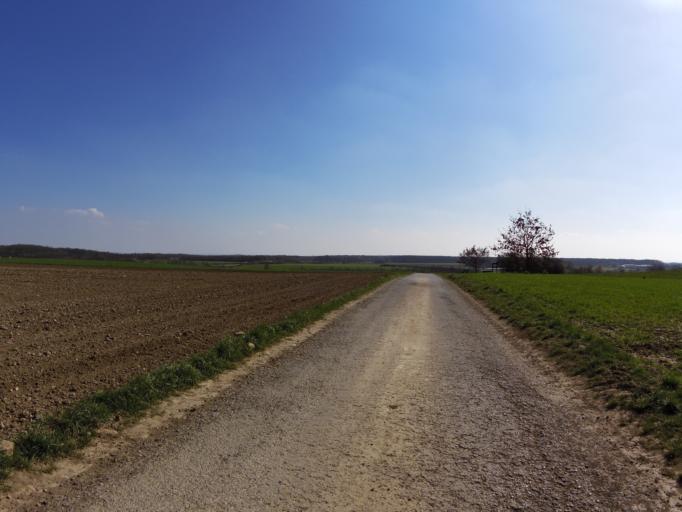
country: DE
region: Bavaria
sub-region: Regierungsbezirk Unterfranken
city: Biebelried
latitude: 49.7394
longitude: 10.1011
